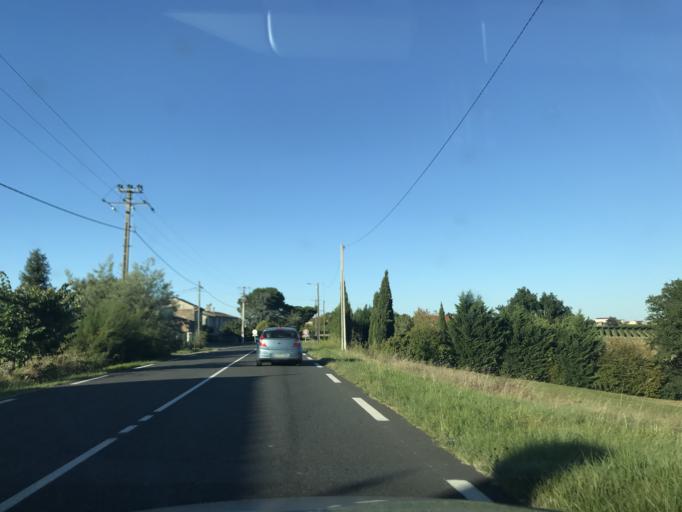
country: FR
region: Aquitaine
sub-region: Departement de la Gironde
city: Saint-Macaire
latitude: 44.5895
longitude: -0.2096
